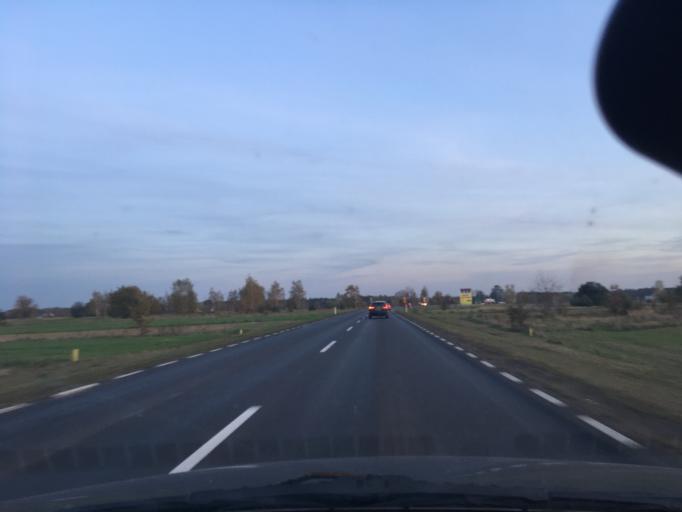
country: PL
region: Masovian Voivodeship
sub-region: Powiat plocki
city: Wyszogrod
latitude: 52.3599
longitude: 20.2038
